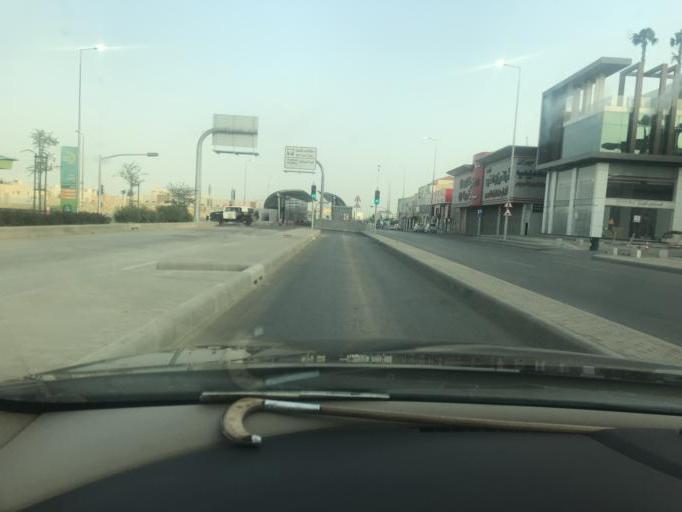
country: SA
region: Ar Riyad
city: Riyadh
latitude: 24.7347
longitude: 46.7837
